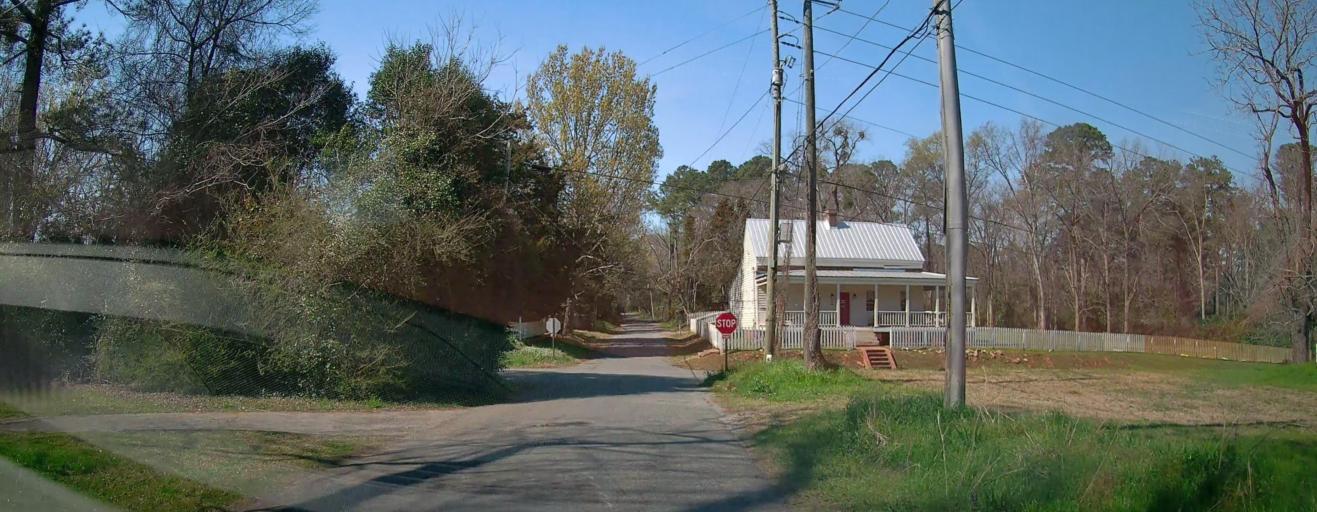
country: US
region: Georgia
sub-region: Jones County
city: Gray
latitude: 32.9993
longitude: -83.5562
